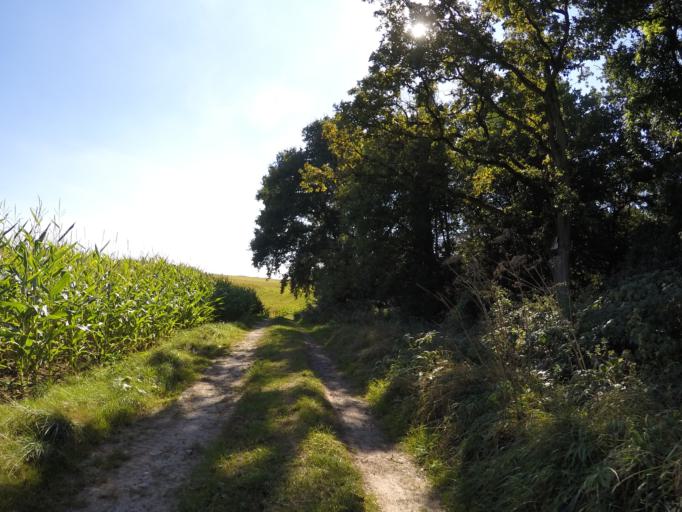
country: BE
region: Wallonia
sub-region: Province de Namur
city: Assesse
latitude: 50.3144
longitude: 5.0302
